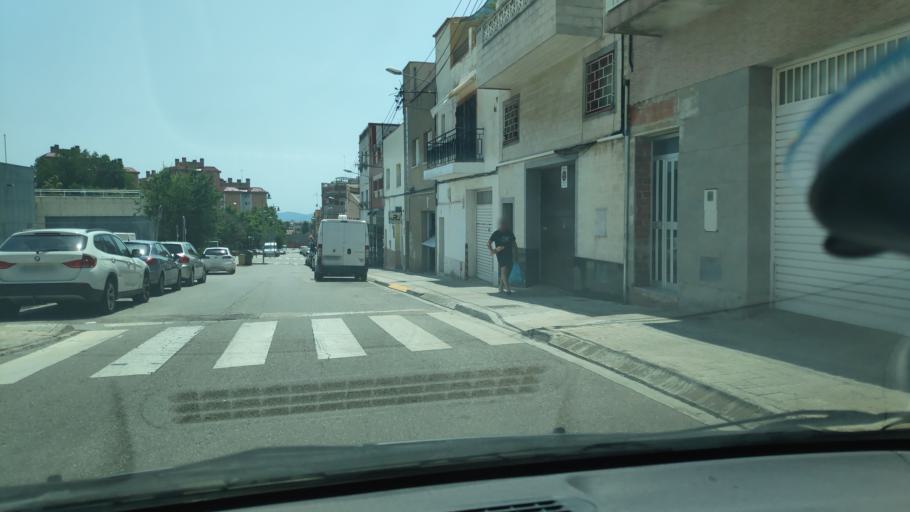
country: ES
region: Catalonia
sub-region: Provincia de Barcelona
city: Terrassa
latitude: 41.5612
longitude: 2.0382
